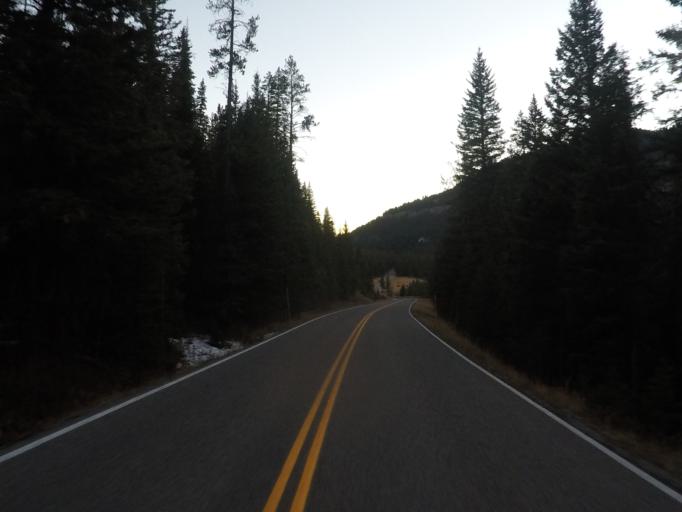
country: US
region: Montana
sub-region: Stillwater County
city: Absarokee
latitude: 44.9549
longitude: -110.0735
